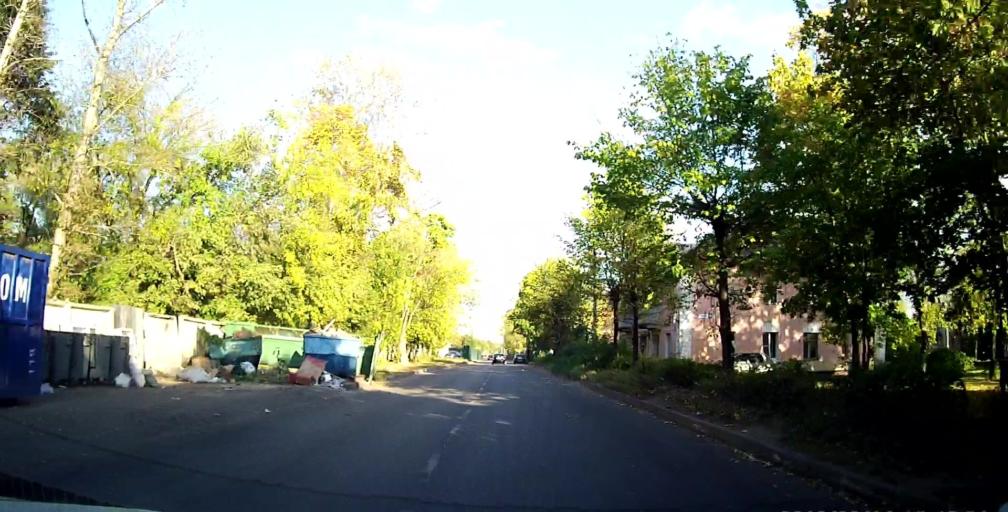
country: RU
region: Moskovskaya
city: Klimovsk
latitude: 55.3681
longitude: 37.5387
